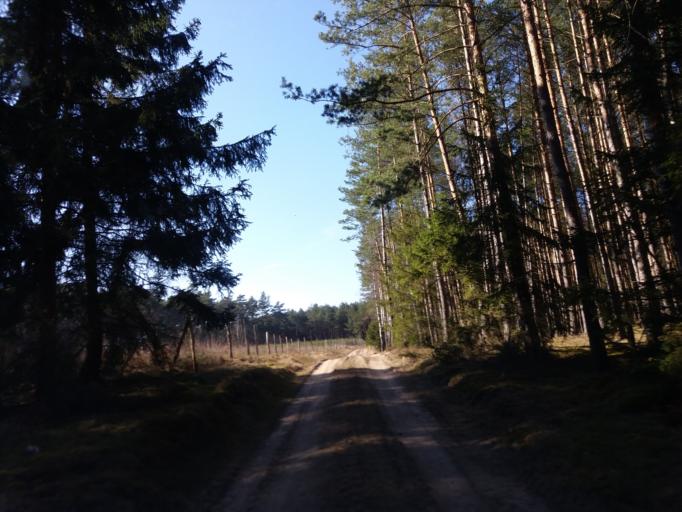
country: PL
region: West Pomeranian Voivodeship
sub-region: Powiat choszczenski
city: Bierzwnik
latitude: 53.1063
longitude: 15.7012
